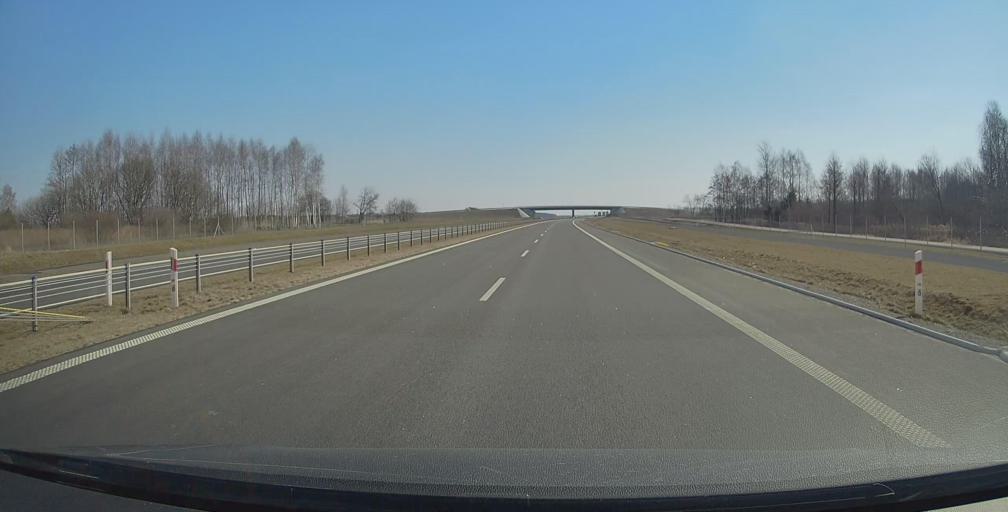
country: PL
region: Lublin Voivodeship
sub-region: Powiat janowski
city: Modliborzyce
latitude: 50.7381
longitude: 22.3325
